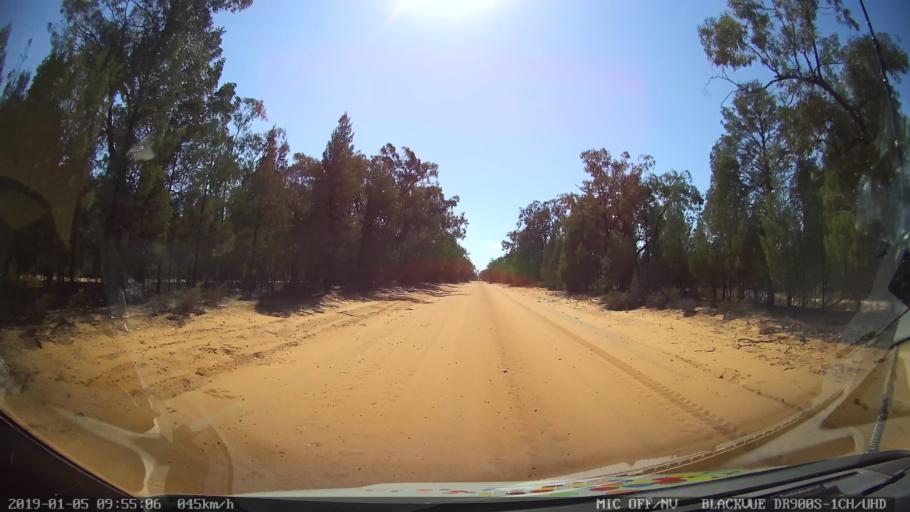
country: AU
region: New South Wales
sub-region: Gilgandra
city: Gilgandra
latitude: -31.6636
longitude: 148.7849
